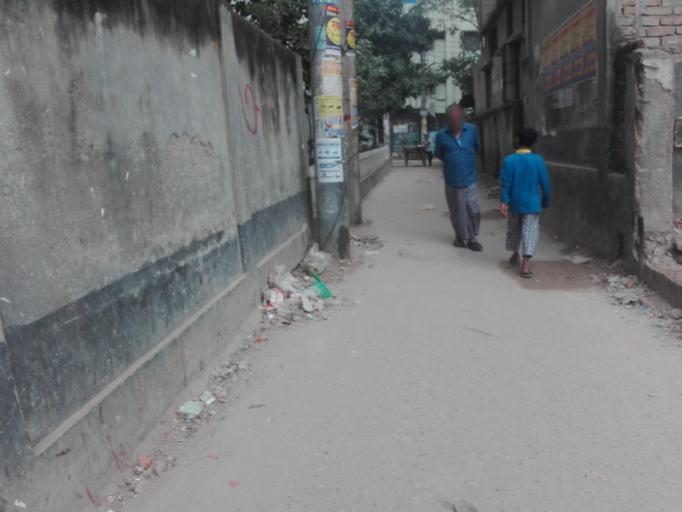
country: BD
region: Dhaka
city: Azimpur
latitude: 23.7929
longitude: 90.3598
